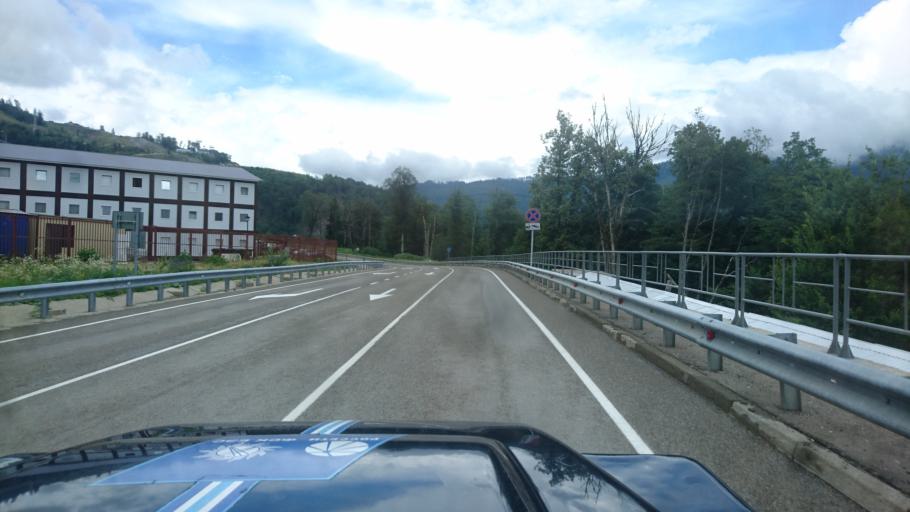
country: RU
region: Krasnodarskiy
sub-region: Sochi City
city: Krasnaya Polyana
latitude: 43.6472
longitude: 40.3402
